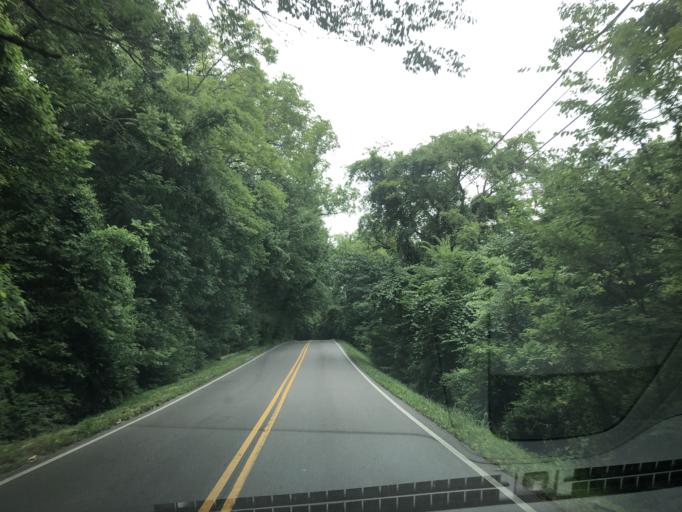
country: US
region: Tennessee
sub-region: Williamson County
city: Nolensville
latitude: 36.0293
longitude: -86.6821
